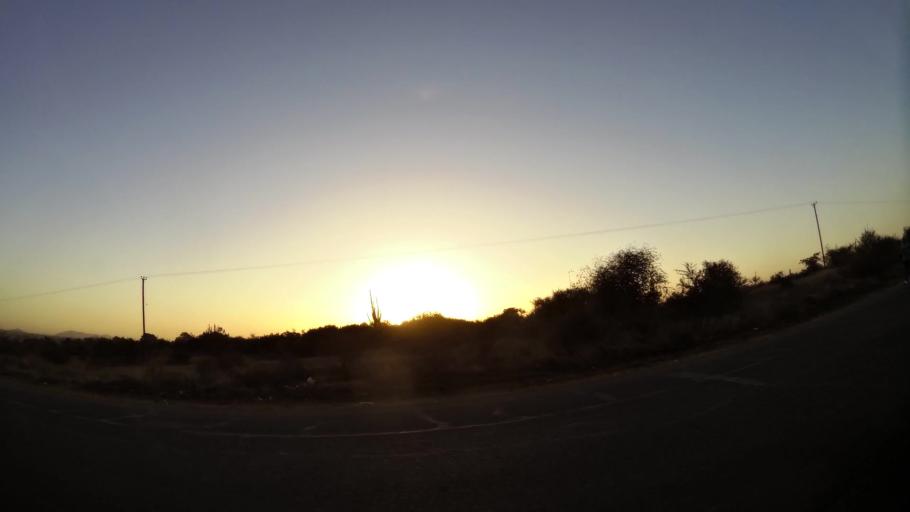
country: ZA
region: North-West
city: Ga-Rankuwa
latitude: -25.5717
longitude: 28.0522
